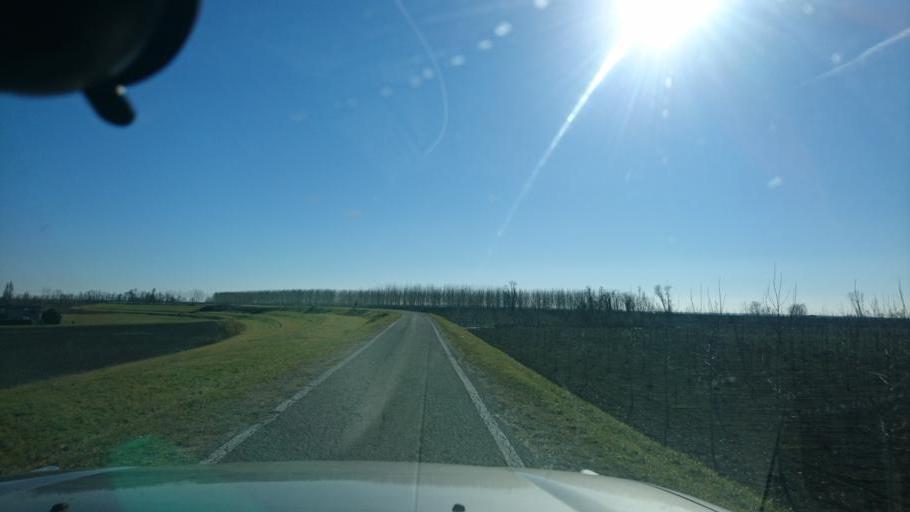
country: IT
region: Veneto
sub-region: Provincia di Rovigo
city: Ariano
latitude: 44.9362
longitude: 12.1301
